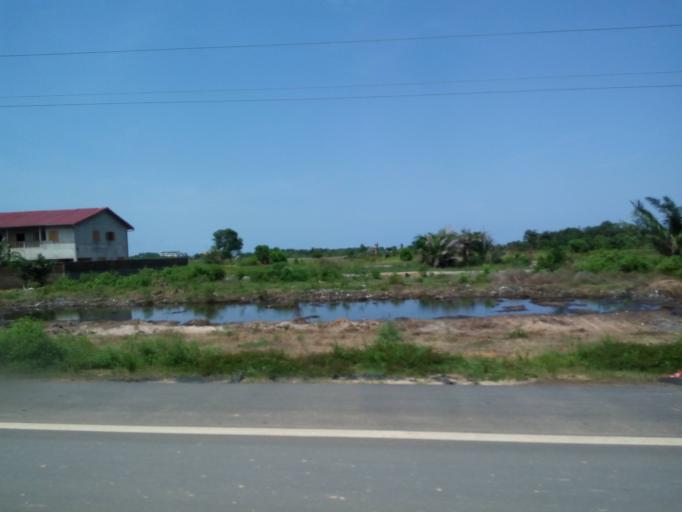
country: CI
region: Sud-Comoe
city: Grand-Bassam
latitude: 5.2302
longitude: -3.7539
